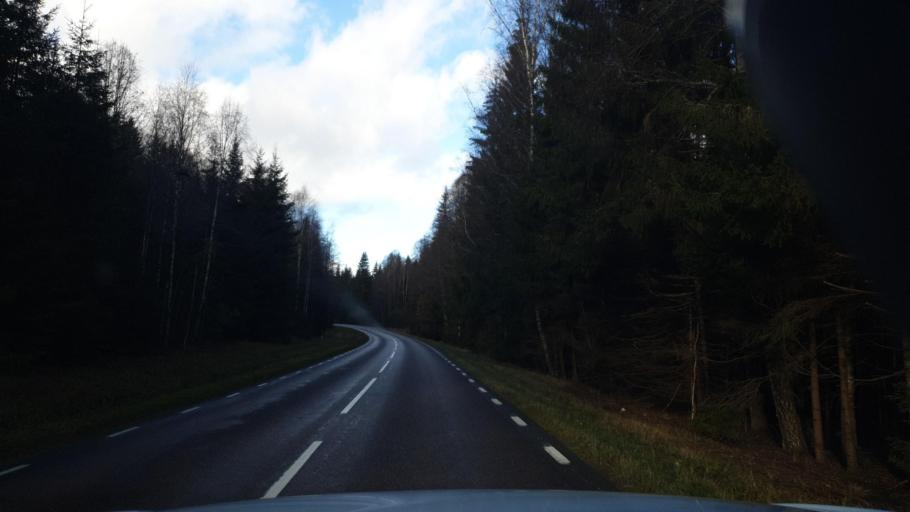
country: SE
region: Vaermland
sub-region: Grums Kommun
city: Slottsbron
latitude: 59.4637
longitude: 12.8307
